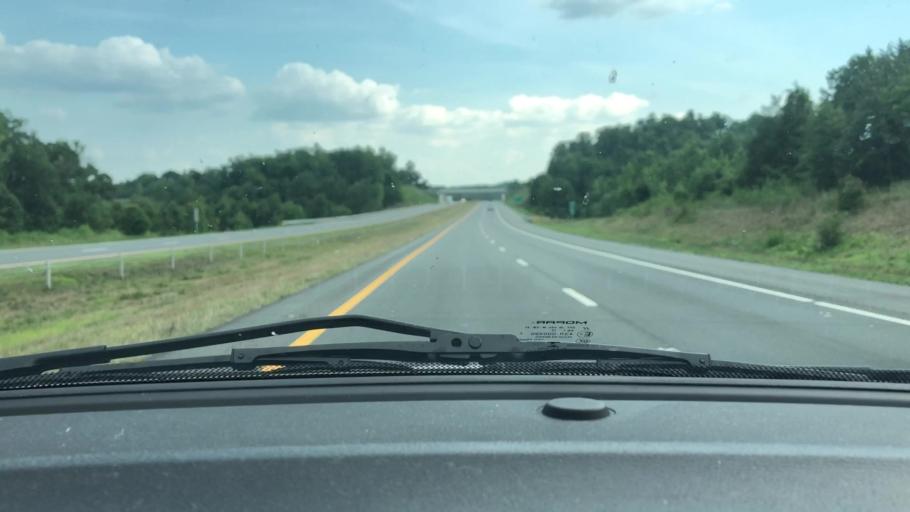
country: US
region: North Carolina
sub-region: Guilford County
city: Summerfield
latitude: 36.1899
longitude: -79.9298
